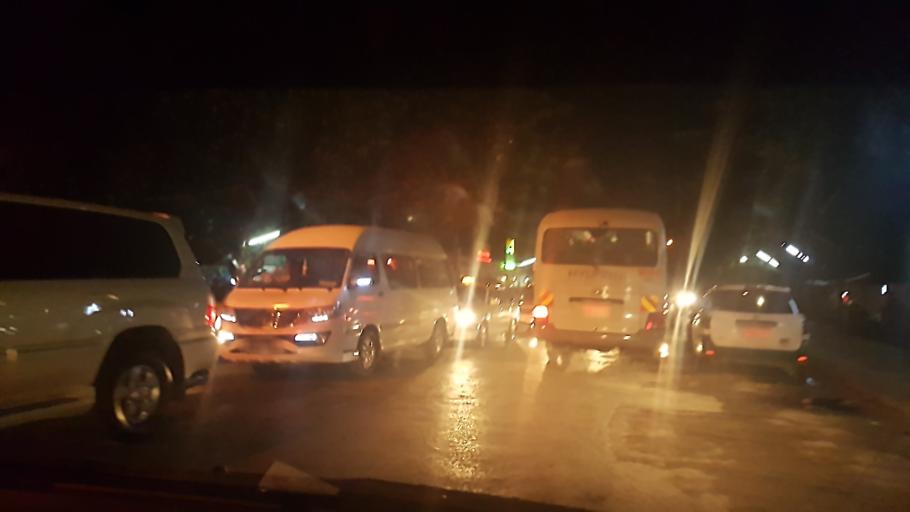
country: MM
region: Yangon
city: Yangon
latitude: 16.8174
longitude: 96.1267
